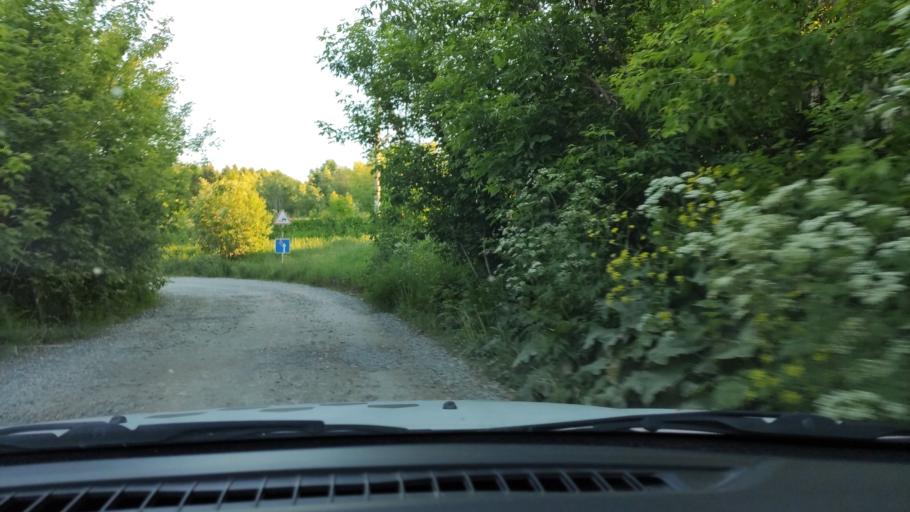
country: RU
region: Perm
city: Sylva
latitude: 58.0437
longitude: 56.7464
